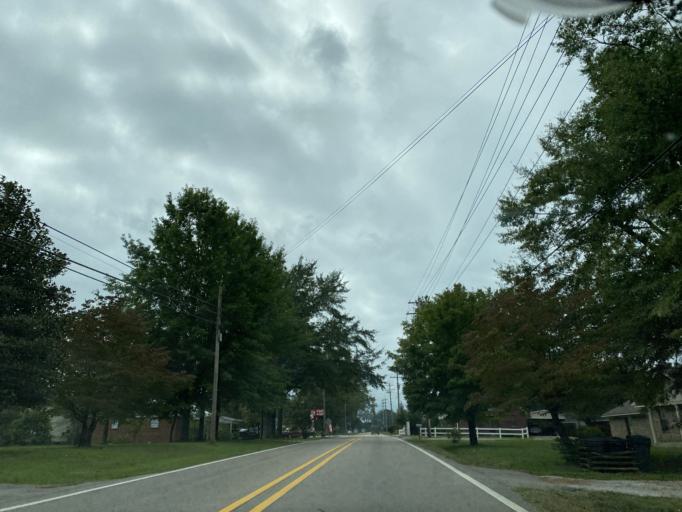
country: US
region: Mississippi
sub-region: Tishomingo County
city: Belmont
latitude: 34.5067
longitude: -88.2070
